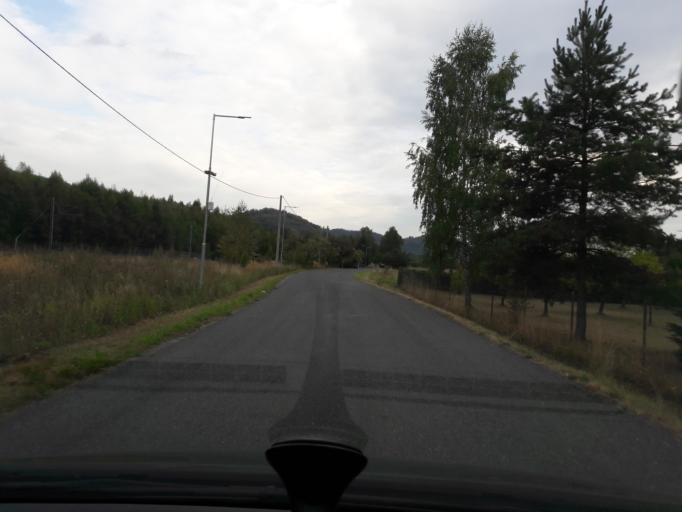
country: CZ
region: Olomoucky
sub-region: Okres Sumperk
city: Loucna nad Desnou
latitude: 50.0611
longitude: 17.0856
